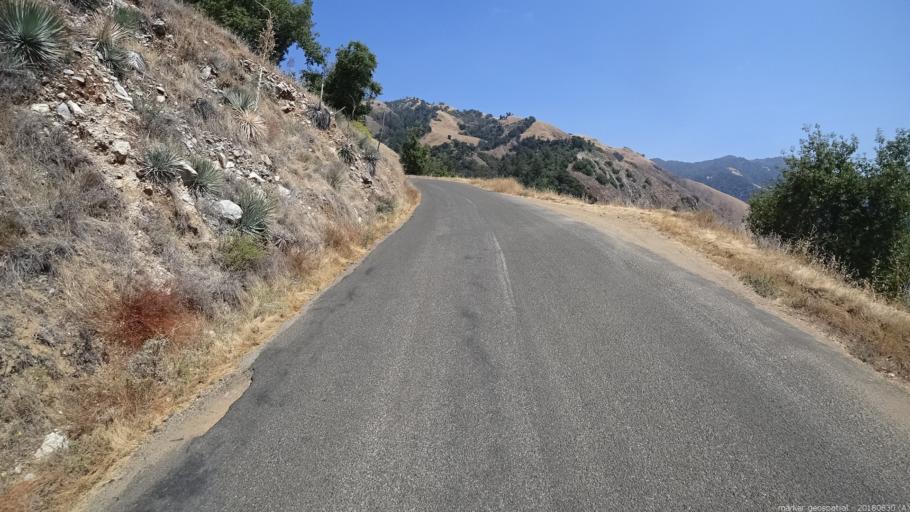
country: US
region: California
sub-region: Monterey County
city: Greenfield
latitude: 35.9978
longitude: -121.4781
